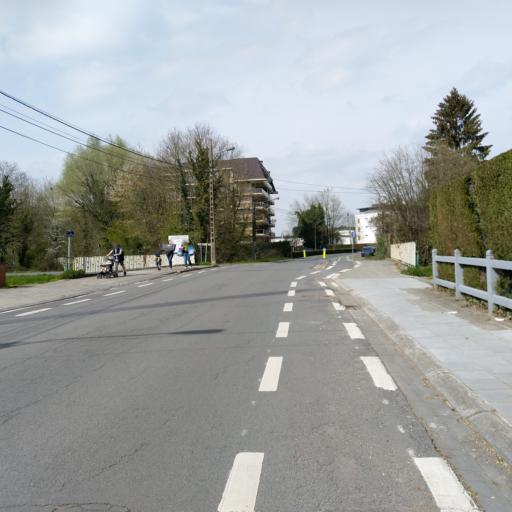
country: BE
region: Wallonia
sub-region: Province du Hainaut
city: Mons
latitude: 50.4428
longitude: 3.9621
